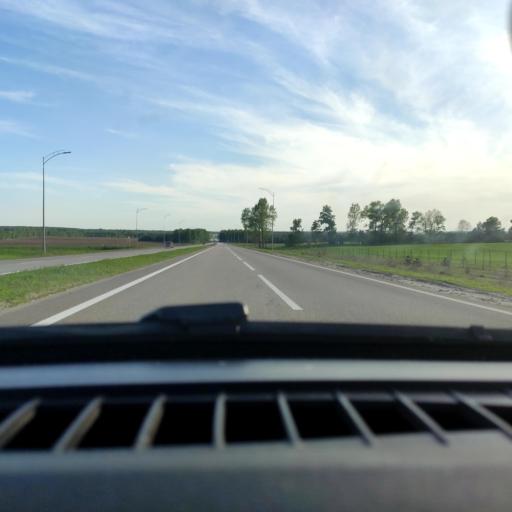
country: RU
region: Belgorod
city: Staryy Oskol
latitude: 51.4178
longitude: 37.8890
